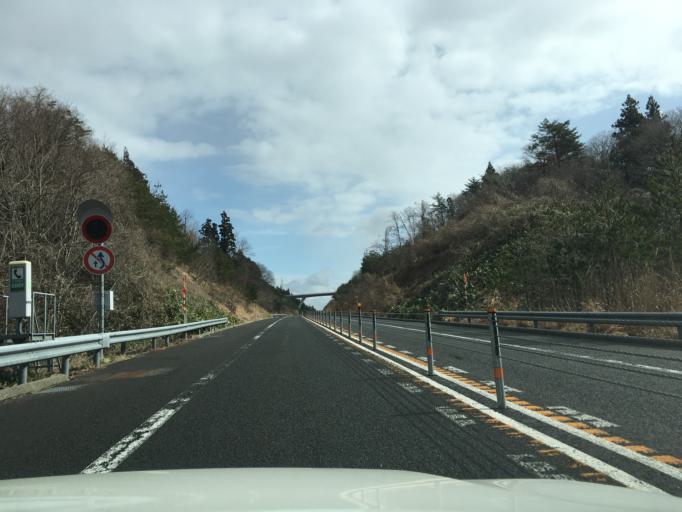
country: JP
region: Akita
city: Akita
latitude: 39.6295
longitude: 140.1638
